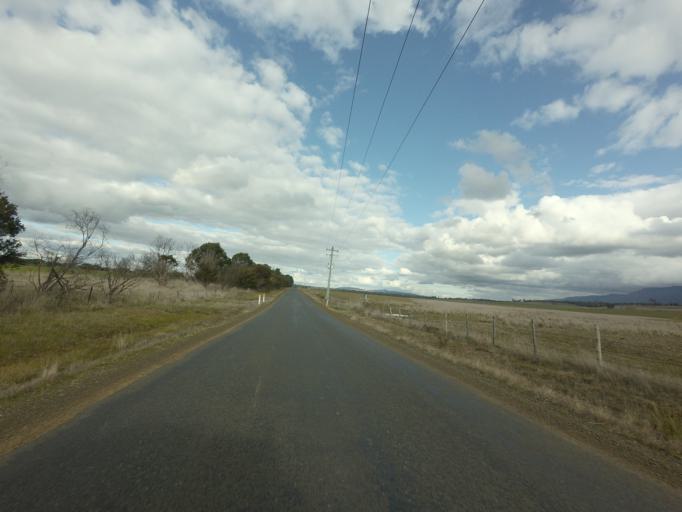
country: AU
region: Tasmania
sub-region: Northern Midlands
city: Longford
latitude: -41.8173
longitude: 147.1967
